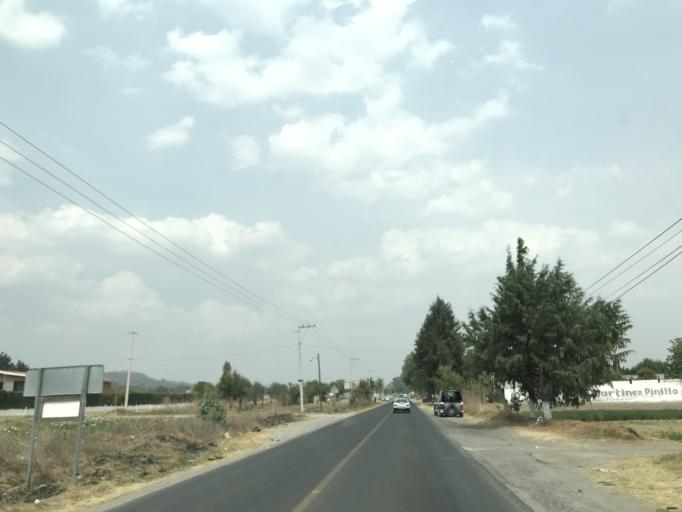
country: MX
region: Tlaxcala
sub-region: Panotla
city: Fraccionamiento la Virgen
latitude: 19.3203
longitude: -98.2858
